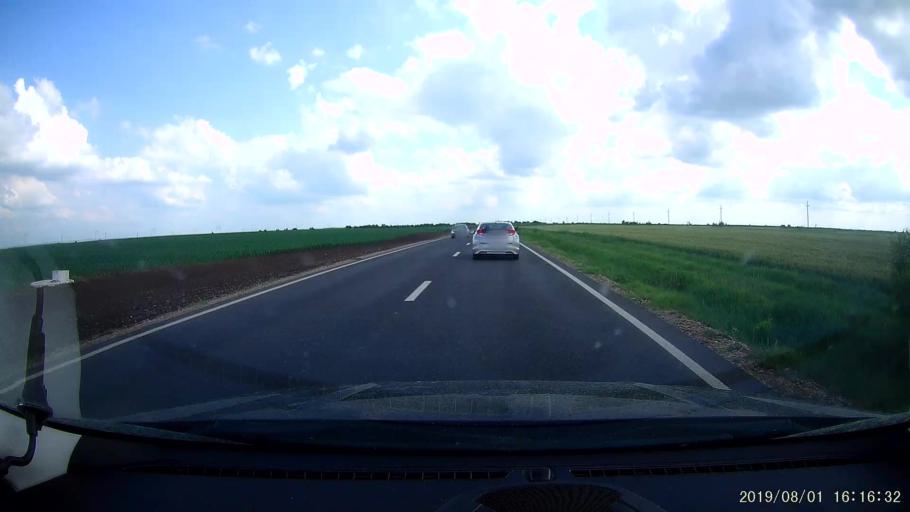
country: RO
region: Calarasi
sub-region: Comuna Stefan Voda
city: Stefan Voda
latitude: 44.3183
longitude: 27.3575
